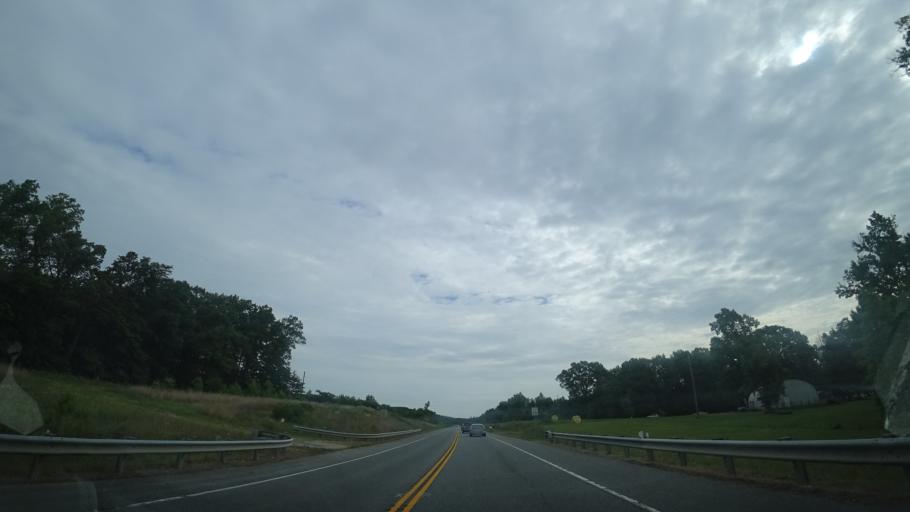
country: US
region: Virginia
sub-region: Spotsylvania County
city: Spotsylvania Courthouse
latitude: 38.1658
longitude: -77.6381
